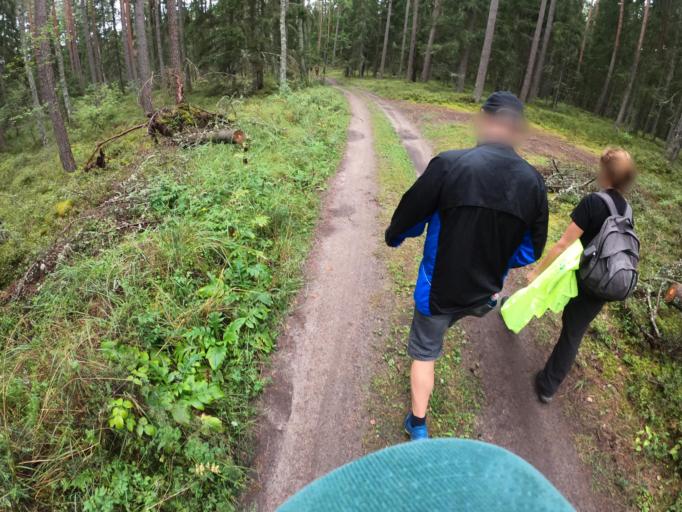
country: LV
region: Engure
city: Smarde
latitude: 56.9915
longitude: 23.3535
